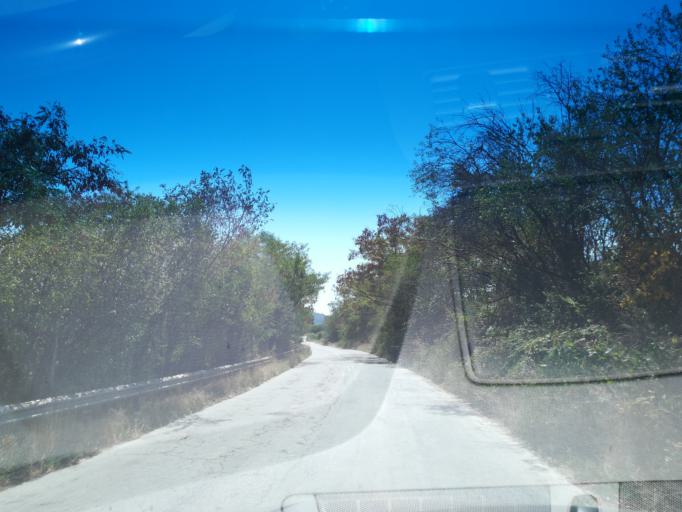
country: BG
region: Pazardzhik
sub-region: Obshtina Strelcha
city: Strelcha
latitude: 42.5211
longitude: 24.3216
